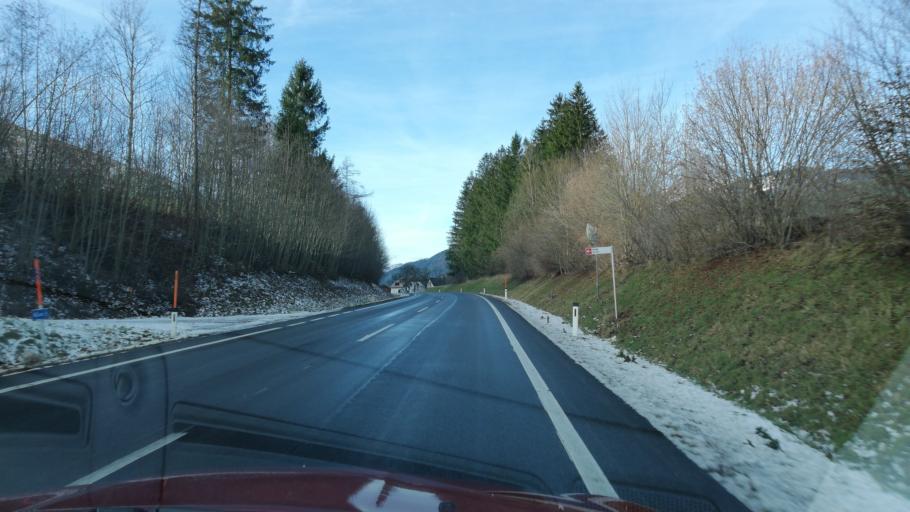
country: AT
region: Upper Austria
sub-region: Politischer Bezirk Kirchdorf an der Krems
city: Rossleithen
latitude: 47.7320
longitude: 14.2892
